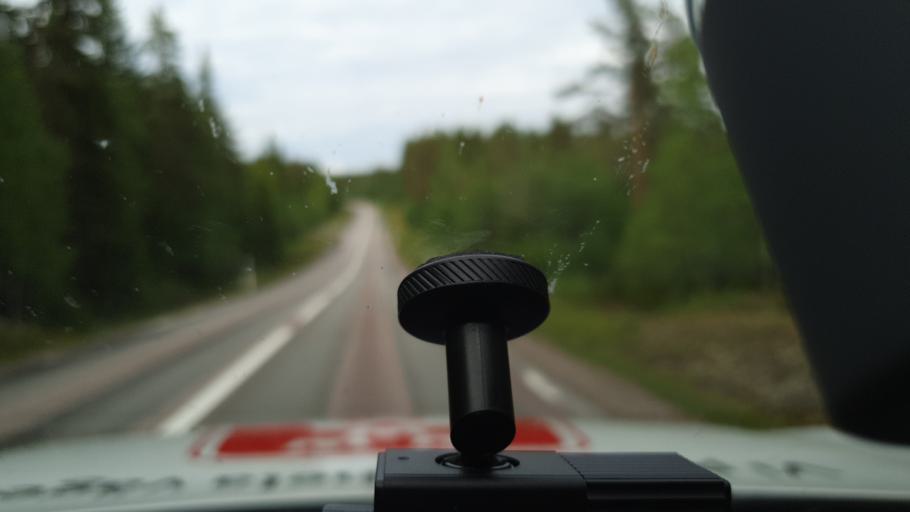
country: SE
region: Vaermland
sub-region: Torsby Kommun
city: Torsby
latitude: 60.3217
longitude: 13.1179
